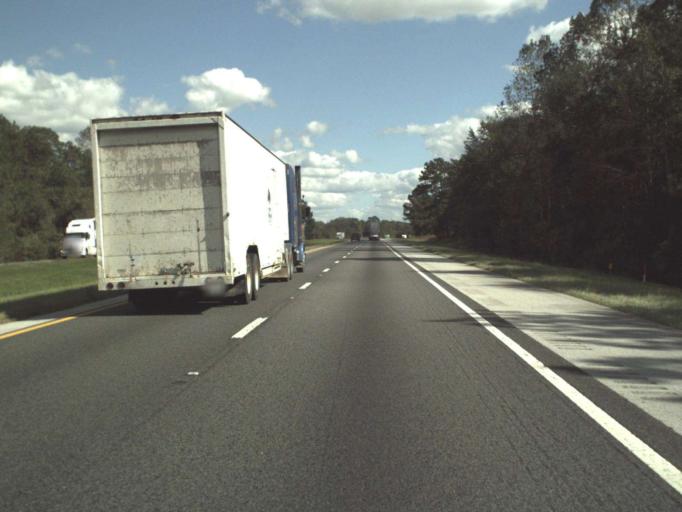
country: US
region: Florida
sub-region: Jackson County
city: Marianna
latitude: 30.6809
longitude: -85.0923
